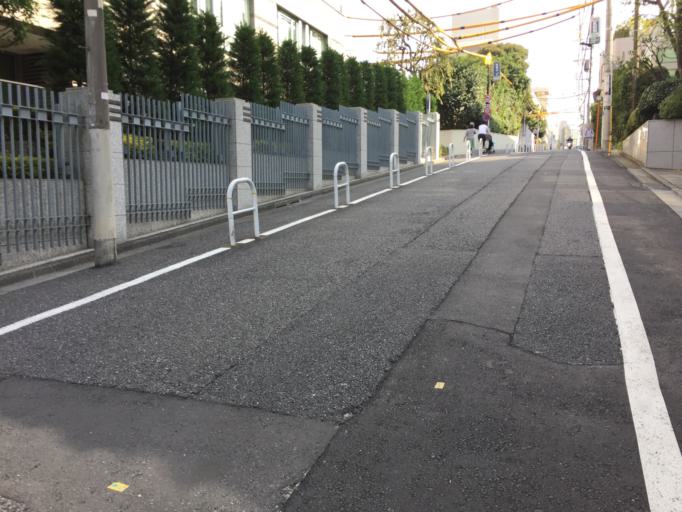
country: JP
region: Tokyo
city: Tokyo
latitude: 35.6411
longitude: 139.7204
